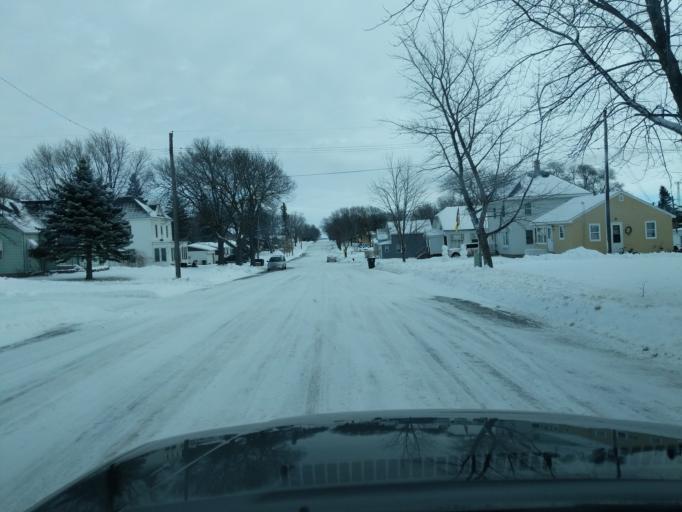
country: US
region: Minnesota
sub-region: Renville County
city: Renville
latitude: 44.7858
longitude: -95.3497
